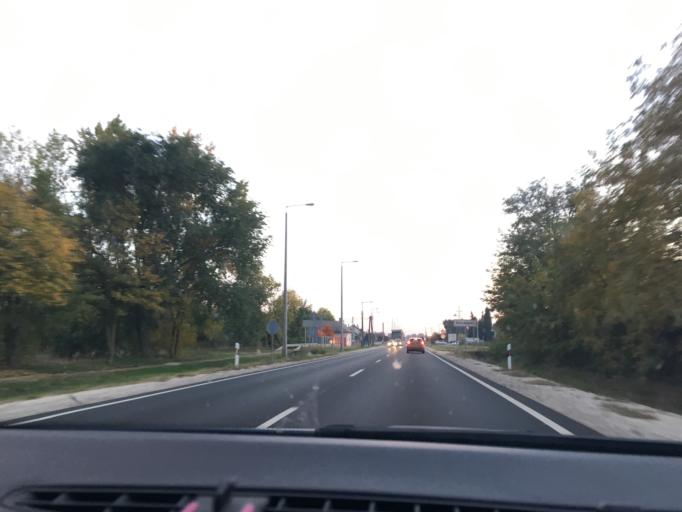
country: HU
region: Hajdu-Bihar
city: Hajduhadhaz
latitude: 47.6504
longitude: 21.6607
